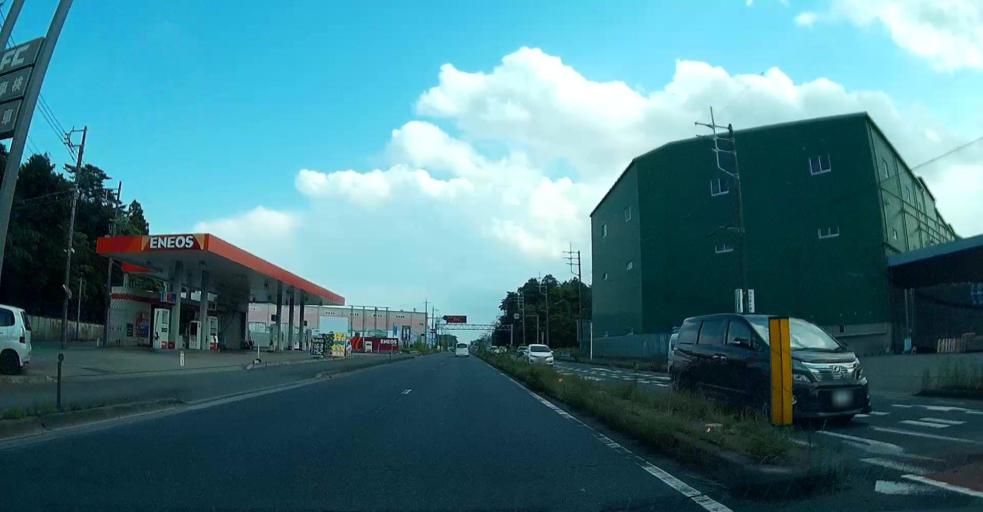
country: JP
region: Chiba
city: Noda
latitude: 35.9744
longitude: 139.8645
